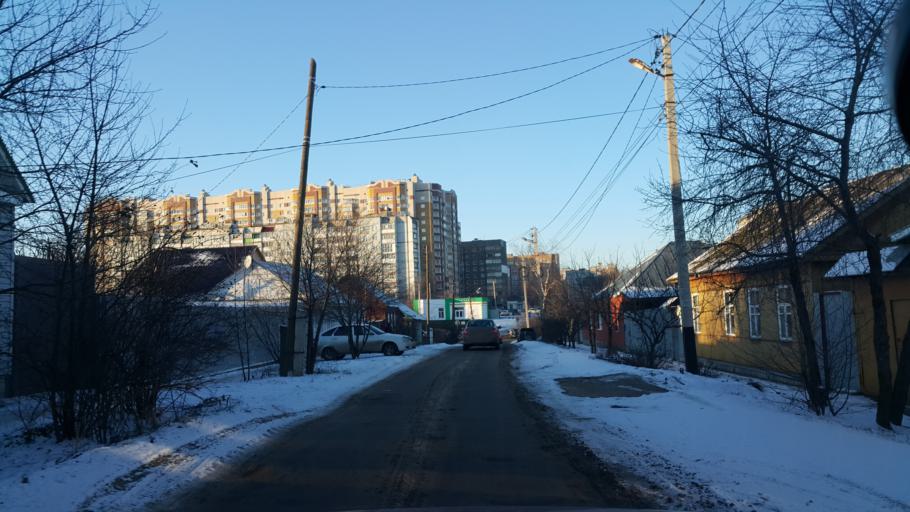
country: RU
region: Tambov
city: Pokrovo-Prigorodnoye
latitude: 52.7025
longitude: 41.4006
